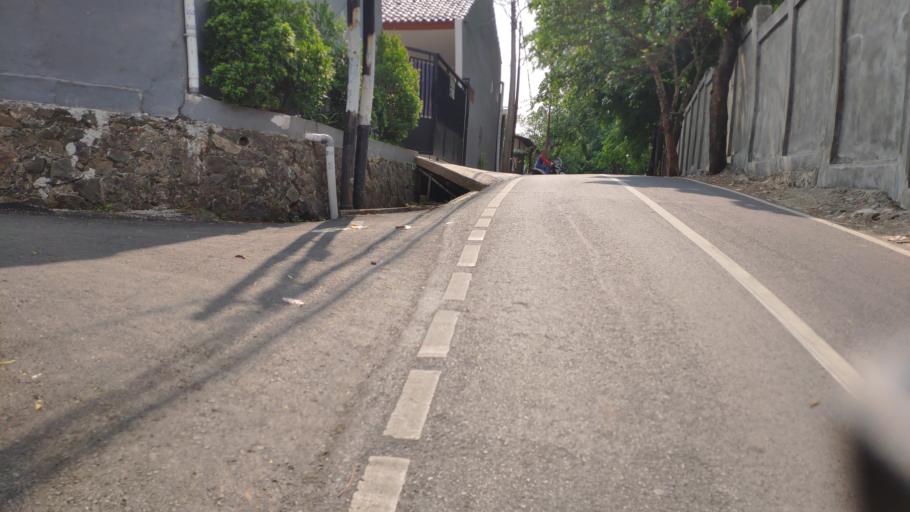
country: ID
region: West Java
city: Depok
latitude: -6.3176
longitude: 106.8220
